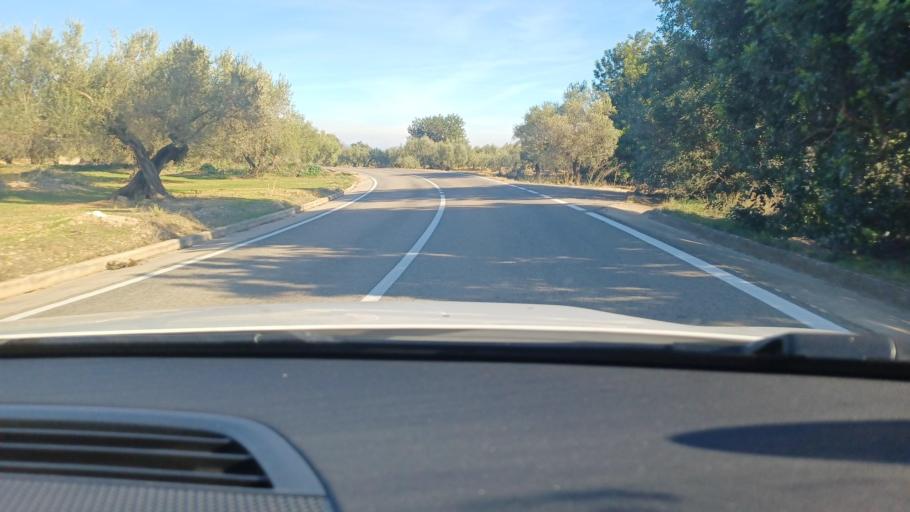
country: ES
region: Catalonia
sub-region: Provincia de Tarragona
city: Mas de Barberans
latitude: 40.7143
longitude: 0.4146
